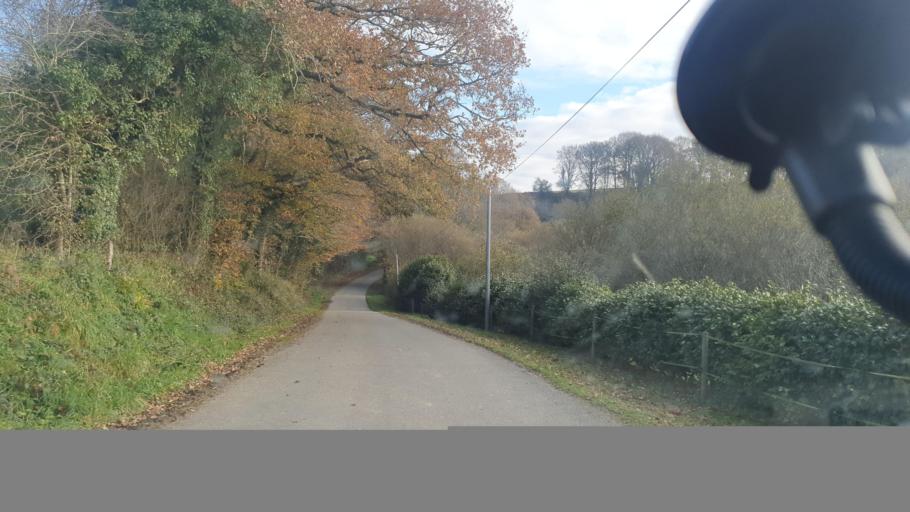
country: FR
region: Brittany
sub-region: Departement du Finistere
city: Landrevarzec
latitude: 48.1043
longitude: -4.0389
